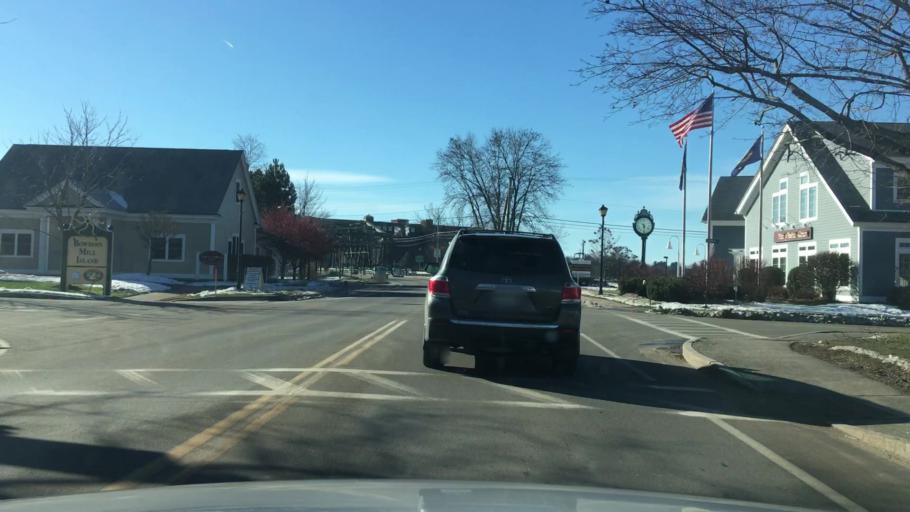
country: US
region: Maine
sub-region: Cumberland County
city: Brunswick
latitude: 43.9232
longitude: -69.9646
